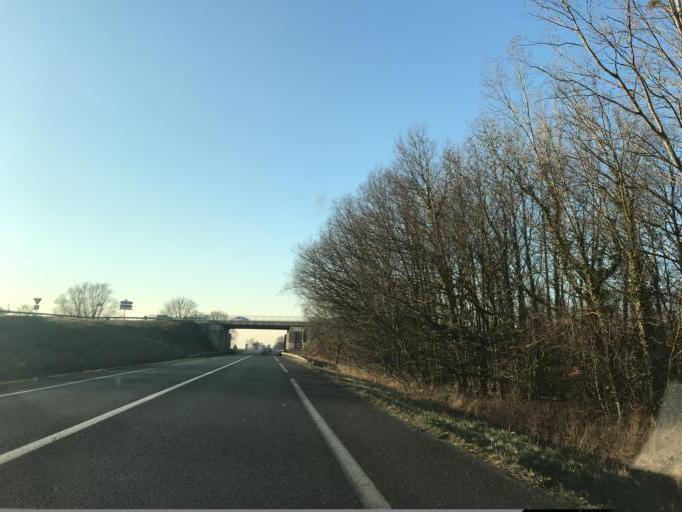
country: FR
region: Ile-de-France
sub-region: Departement de Seine-et-Marne
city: Villiers-sur-Morin
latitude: 48.8551
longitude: 2.8580
